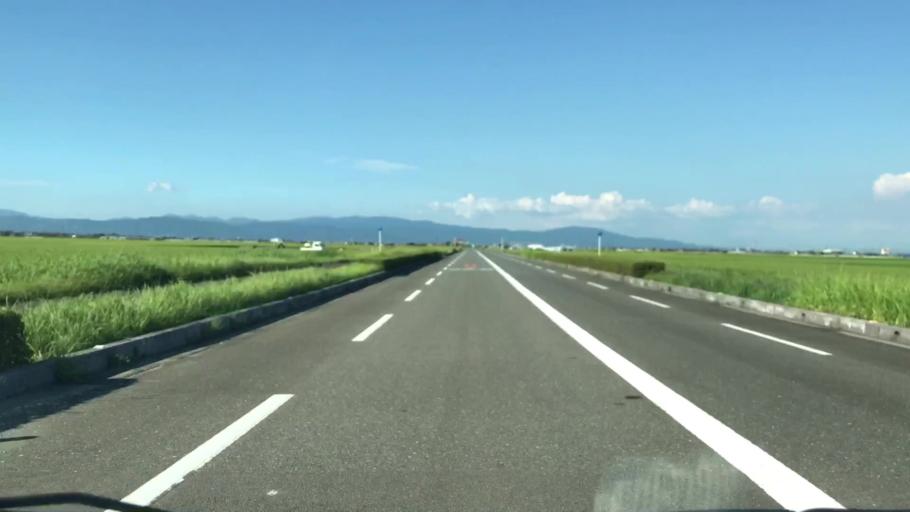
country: JP
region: Saga Prefecture
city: Okawa
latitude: 33.1732
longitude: 130.2958
